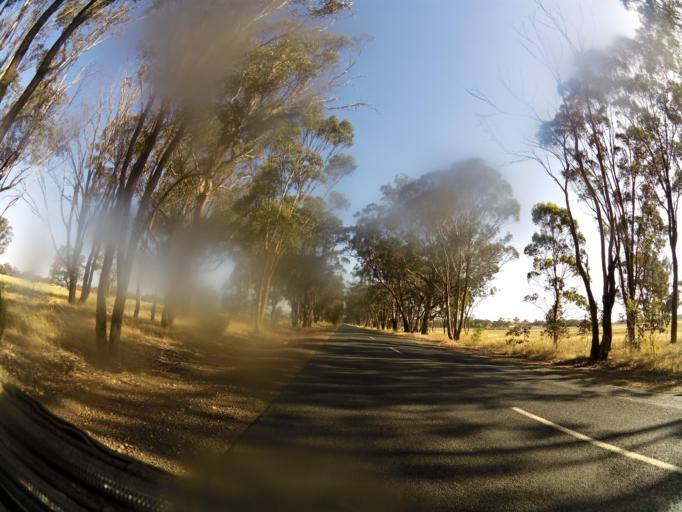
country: AU
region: Victoria
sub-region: Murrindindi
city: Kinglake West
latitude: -36.9781
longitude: 145.1103
